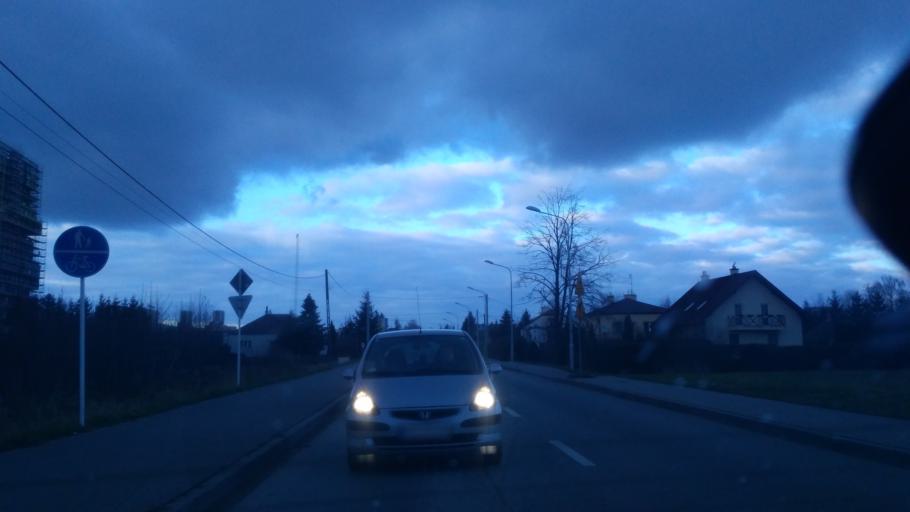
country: PL
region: Subcarpathian Voivodeship
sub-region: Rzeszow
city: Rzeszow
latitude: 50.0270
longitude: 22.0423
